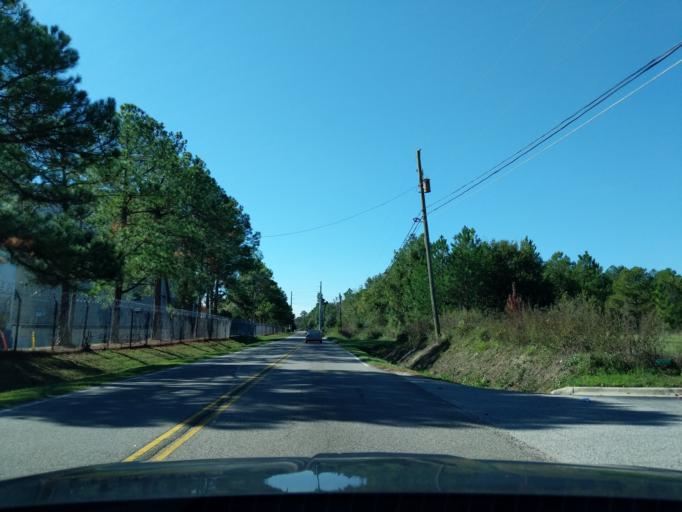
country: US
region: Georgia
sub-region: Richmond County
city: Augusta
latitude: 33.4364
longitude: -82.0015
